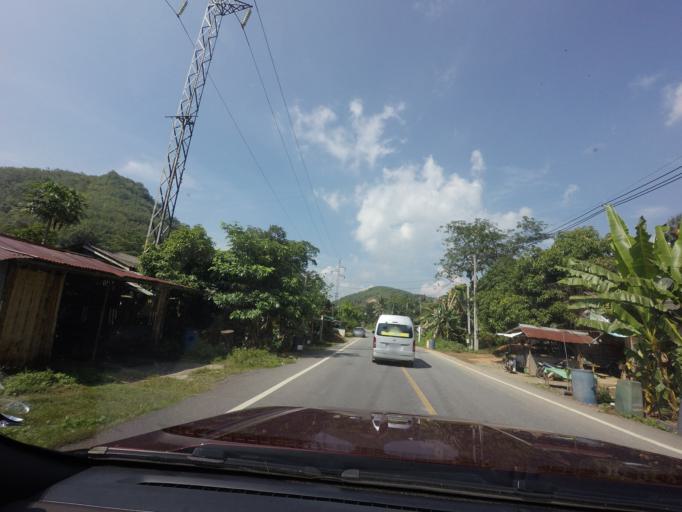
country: TH
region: Yala
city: Betong
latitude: 5.9394
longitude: 101.1872
